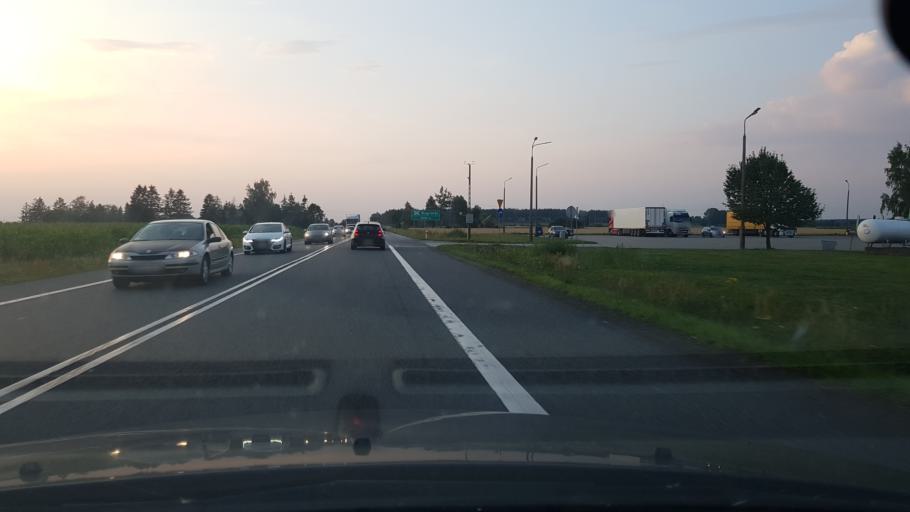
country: PL
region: Masovian Voivodeship
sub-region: Powiat mlawski
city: Wieczfnia Koscielna
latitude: 53.2003
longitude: 20.4358
